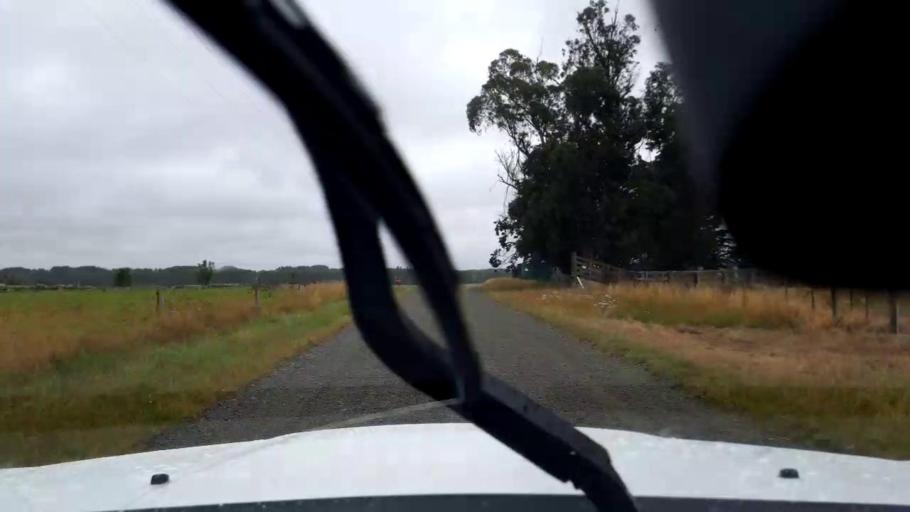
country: NZ
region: Canterbury
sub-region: Timaru District
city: Pleasant Point
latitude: -44.2504
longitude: 171.2005
